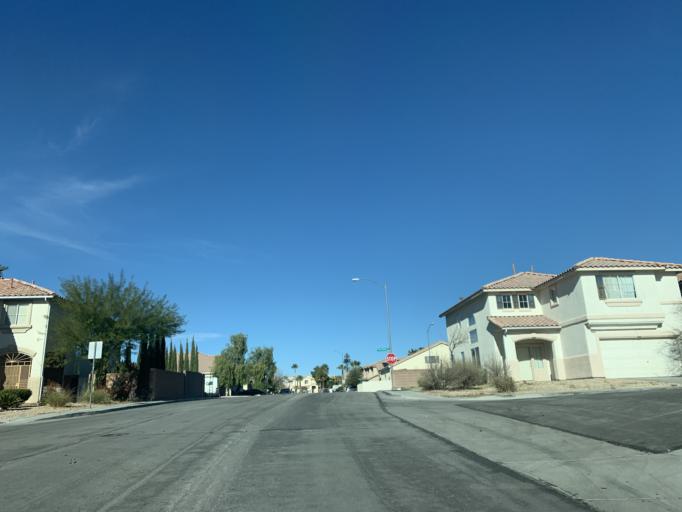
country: US
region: Nevada
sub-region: Clark County
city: Summerlin South
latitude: 36.1255
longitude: -115.2985
